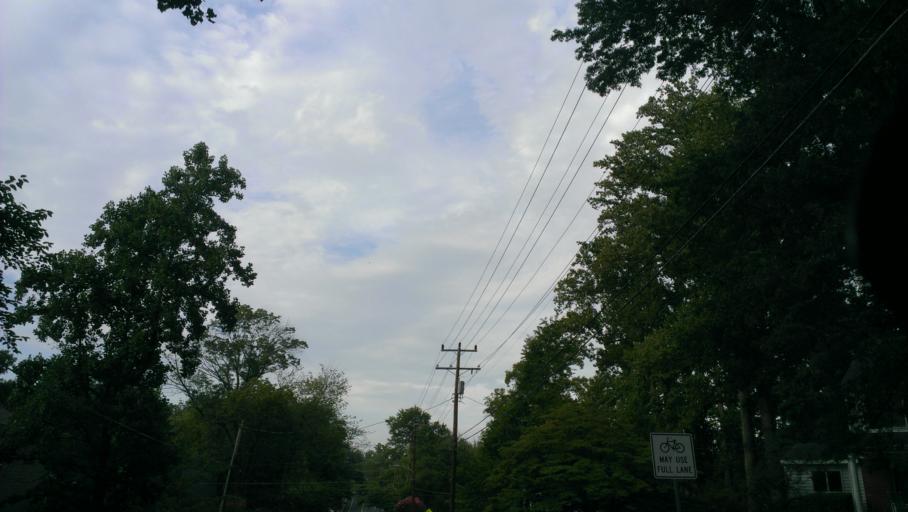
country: US
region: Virginia
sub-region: Fairfax County
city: Idylwood
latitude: 38.8866
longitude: -77.1935
